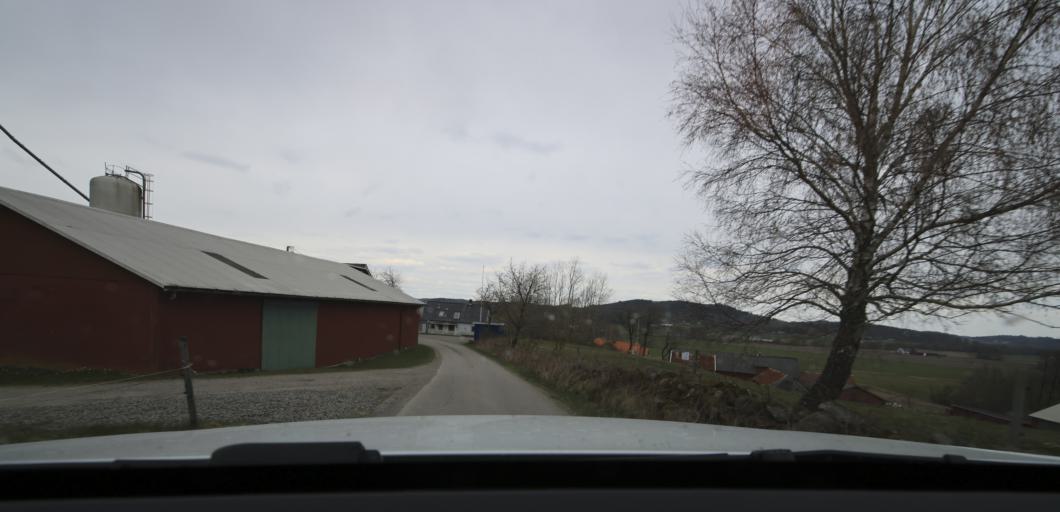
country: SE
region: Halland
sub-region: Varbergs Kommun
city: Tvaaker
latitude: 57.1288
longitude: 12.4579
